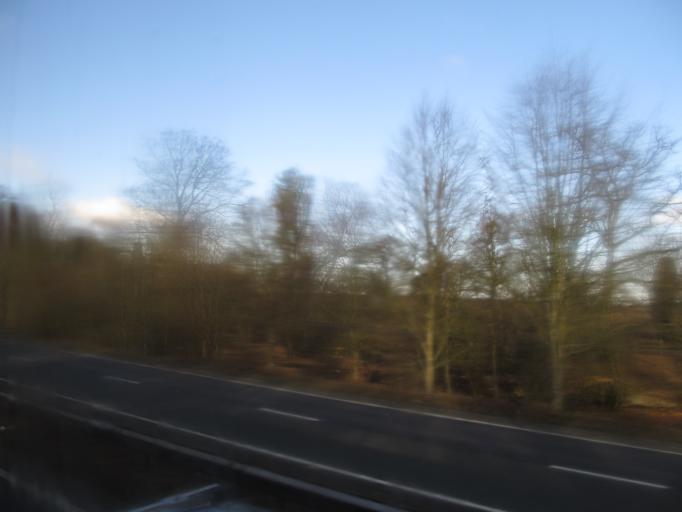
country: GB
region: England
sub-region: Hampshire
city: Overton
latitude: 51.1910
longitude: -1.2451
